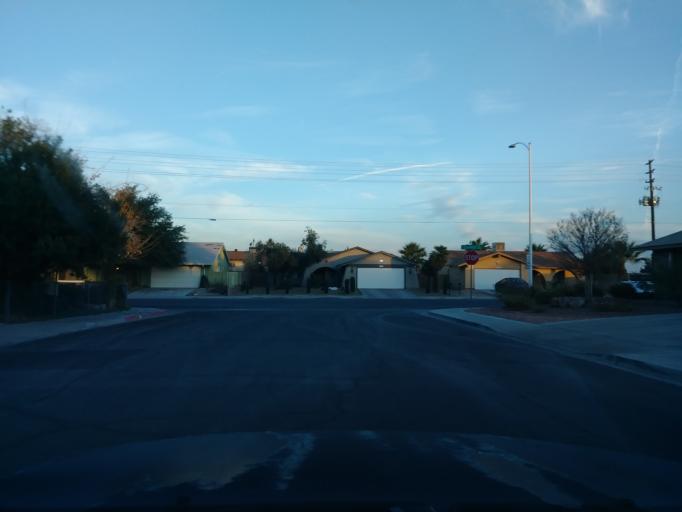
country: US
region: Nevada
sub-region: Clark County
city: Spring Valley
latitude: 36.1716
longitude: -115.2427
